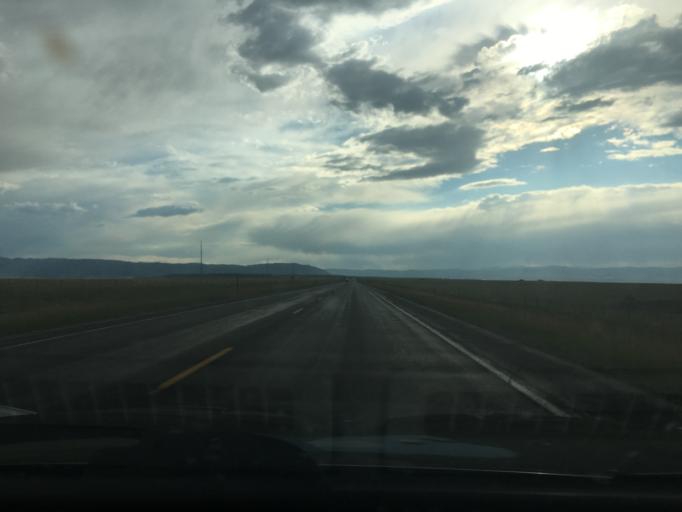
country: US
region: Wyoming
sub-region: Albany County
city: Laramie
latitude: 41.3092
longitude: -105.8195
